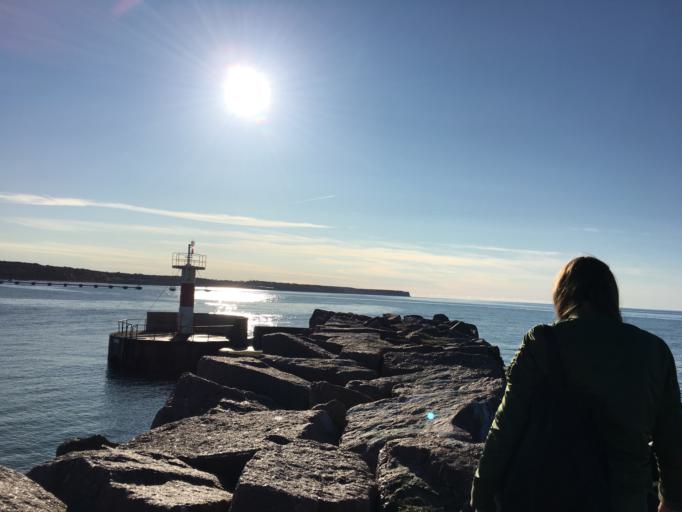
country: SE
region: Gotland
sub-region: Gotland
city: Visby
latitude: 57.6351
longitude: 18.2704
